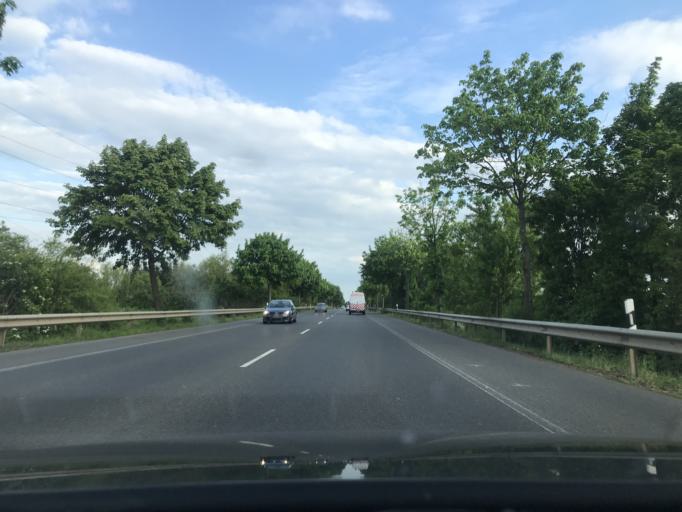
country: DE
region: North Rhine-Westphalia
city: Bornheim
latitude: 50.7751
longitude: 6.9971
